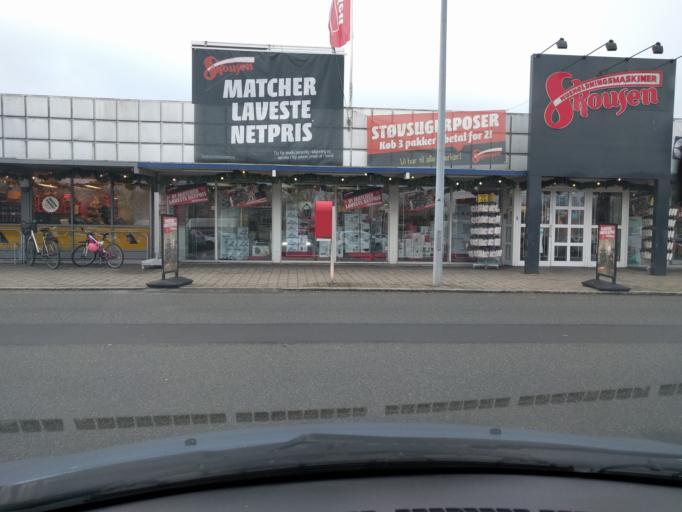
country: DK
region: South Denmark
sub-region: Odense Kommune
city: Neder Holluf
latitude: 55.3788
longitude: 10.4332
